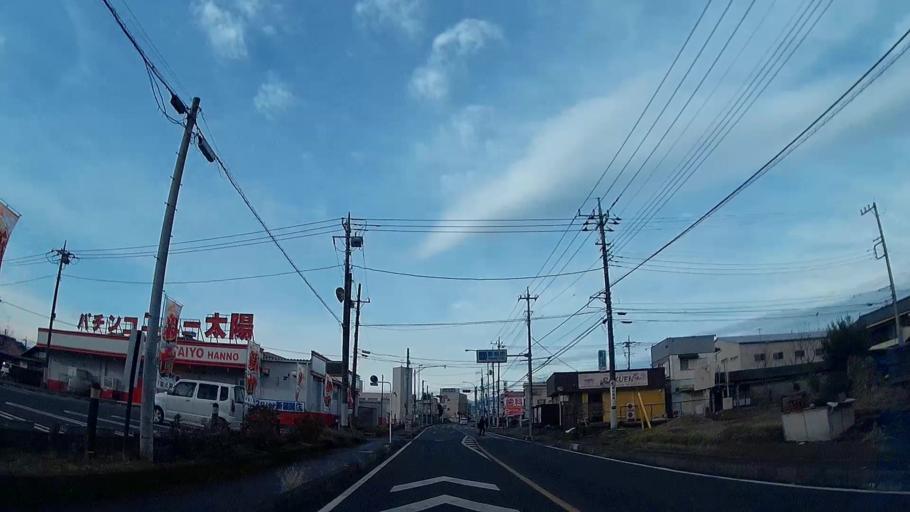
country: JP
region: Saitama
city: Hanno
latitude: 35.8451
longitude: 139.3458
